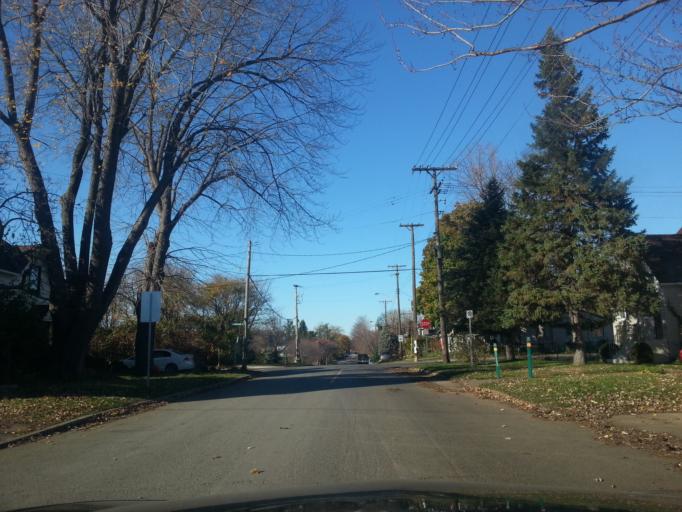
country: CA
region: Ontario
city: Ottawa
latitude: 45.3830
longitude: -75.7519
